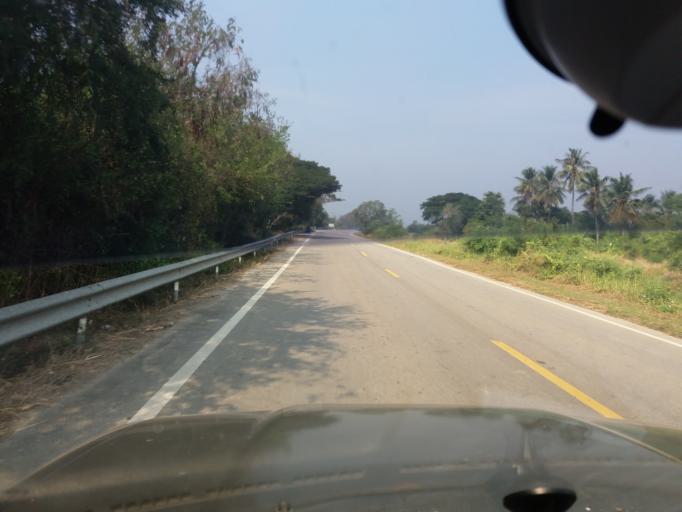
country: TH
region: Sing Buri
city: Bang Racham
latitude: 14.9077
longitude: 100.2606
